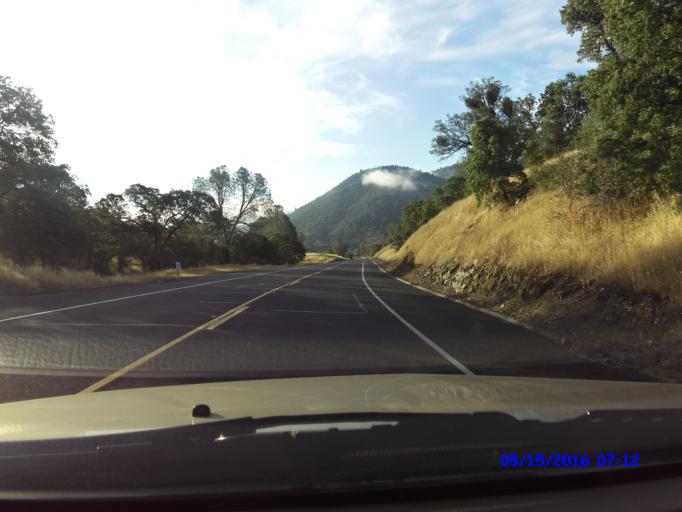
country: US
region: California
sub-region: Tuolumne County
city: Jamestown
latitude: 37.8486
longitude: -120.3887
